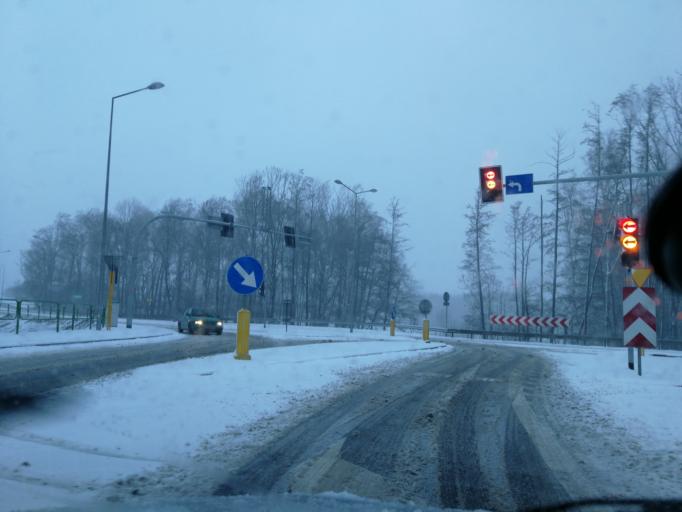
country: PL
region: Silesian Voivodeship
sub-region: Powiat pszczynski
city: Radostowice
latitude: 49.9977
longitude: 18.8936
